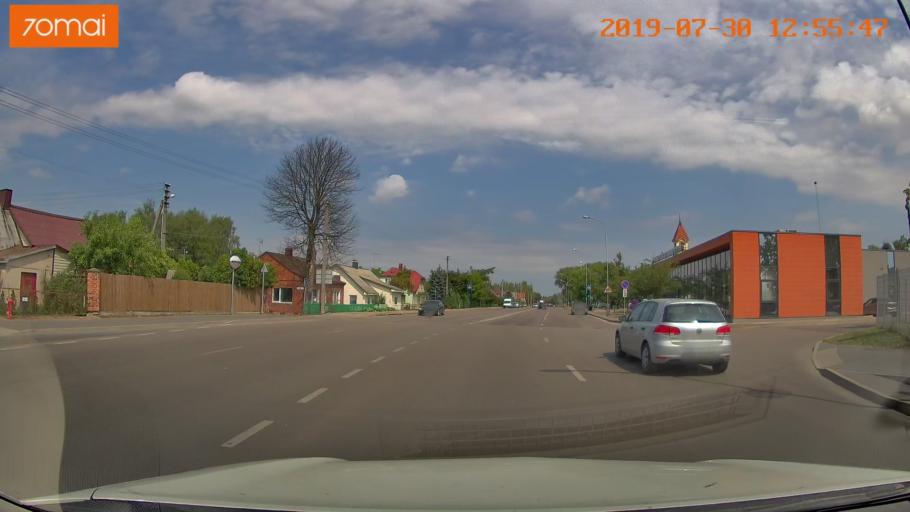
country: LT
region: Marijampoles apskritis
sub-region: Marijampole Municipality
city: Marijampole
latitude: 54.5563
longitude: 23.3629
